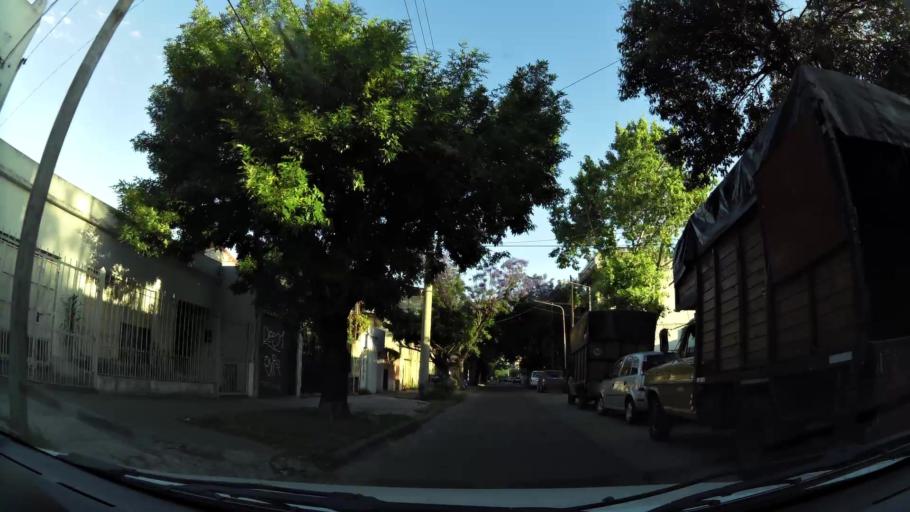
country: AR
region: Buenos Aires
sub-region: Partido de General San Martin
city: General San Martin
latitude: -34.5675
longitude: -58.5256
